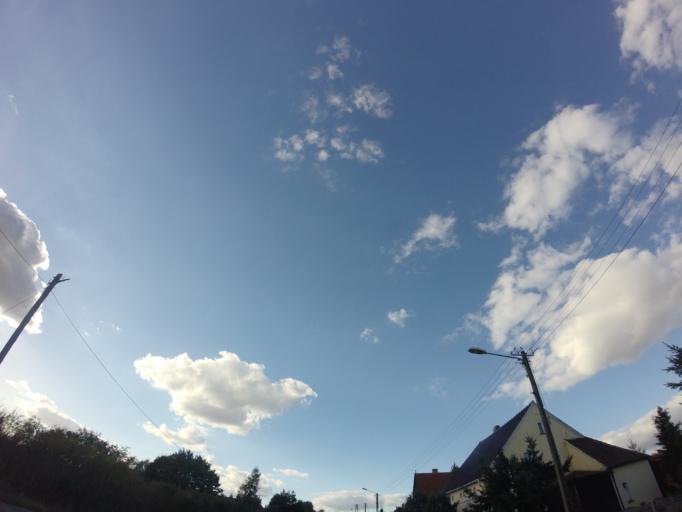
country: PL
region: Greater Poland Voivodeship
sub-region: Powiat nowotomyski
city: Nowy Tomysl
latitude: 52.2702
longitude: 16.1299
